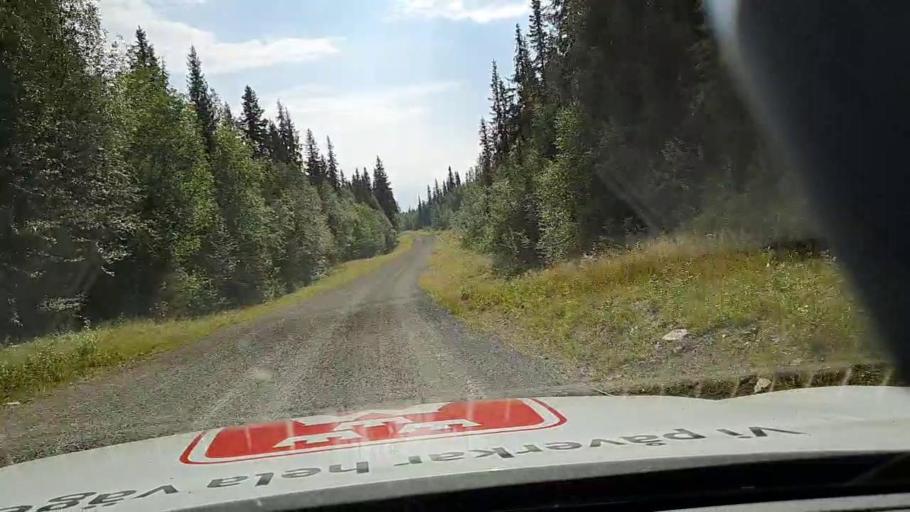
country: SE
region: Vaesterbotten
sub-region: Storumans Kommun
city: Fristad
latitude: 65.5371
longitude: 16.8096
